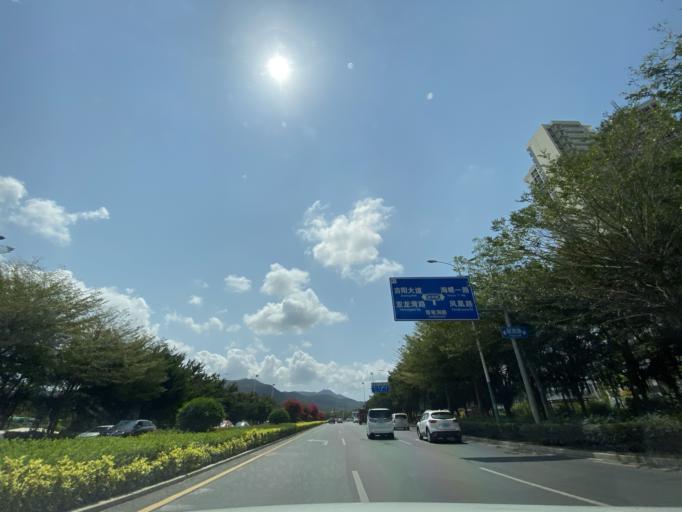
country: CN
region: Hainan
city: Tiandu
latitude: 18.2944
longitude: 109.5289
